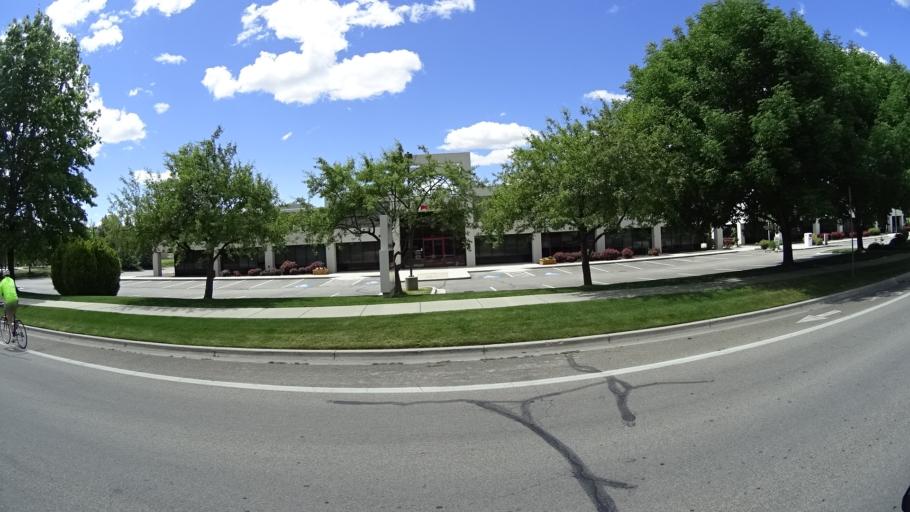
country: US
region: Idaho
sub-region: Ada County
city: Eagle
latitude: 43.6608
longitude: -116.3416
